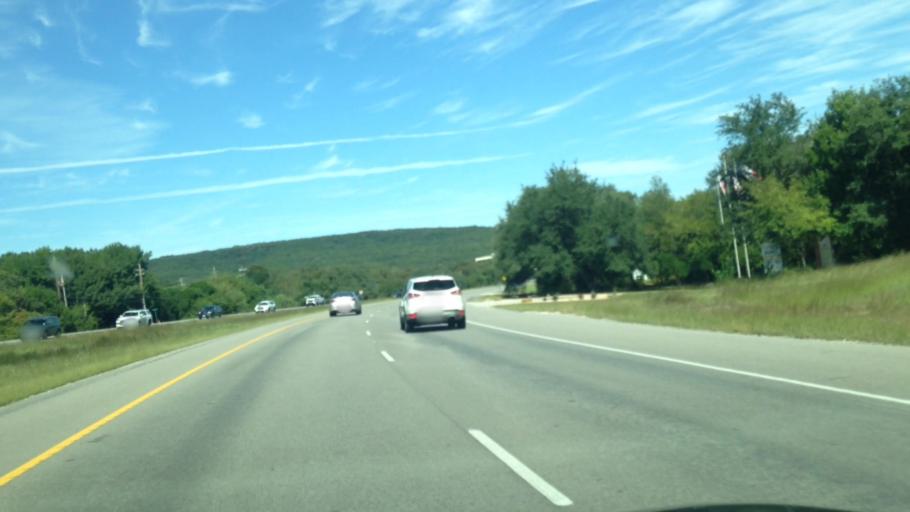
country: US
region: Texas
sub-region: Travis County
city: West Lake Hills
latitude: 30.3680
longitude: -97.7885
